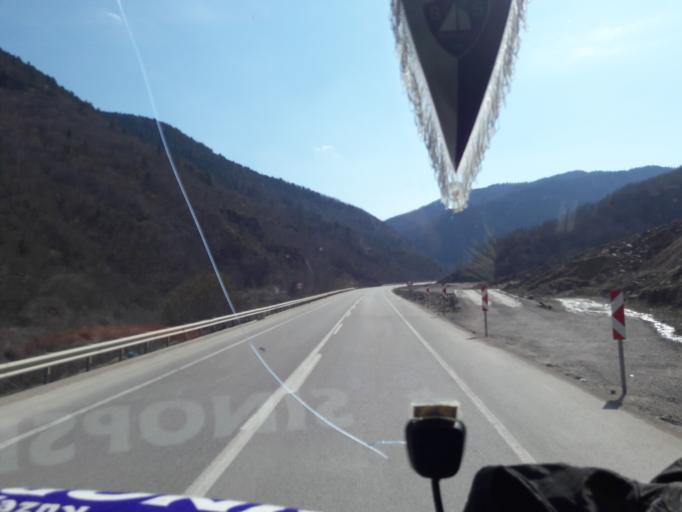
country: TR
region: Sinop
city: Erfelek
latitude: 41.7029
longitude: 34.9158
